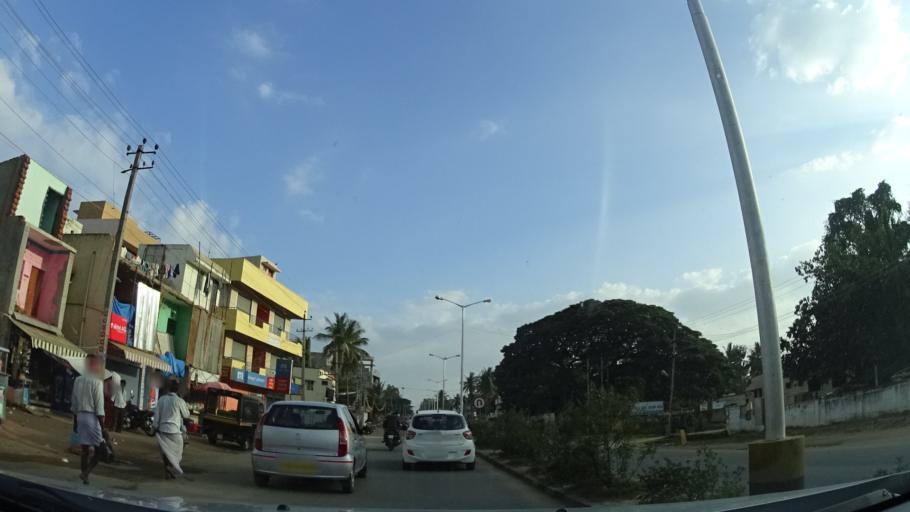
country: IN
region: Karnataka
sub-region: Mandya
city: Malavalli
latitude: 12.3838
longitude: 77.0607
